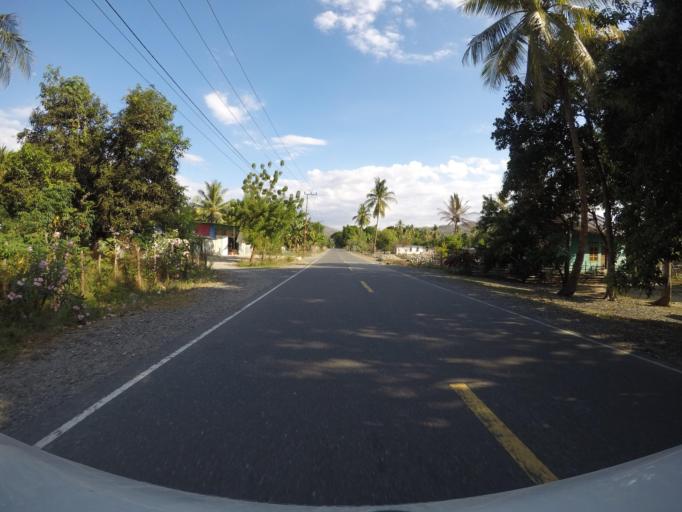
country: TL
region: Liquica
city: Maubara
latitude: -8.7327
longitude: 125.1362
